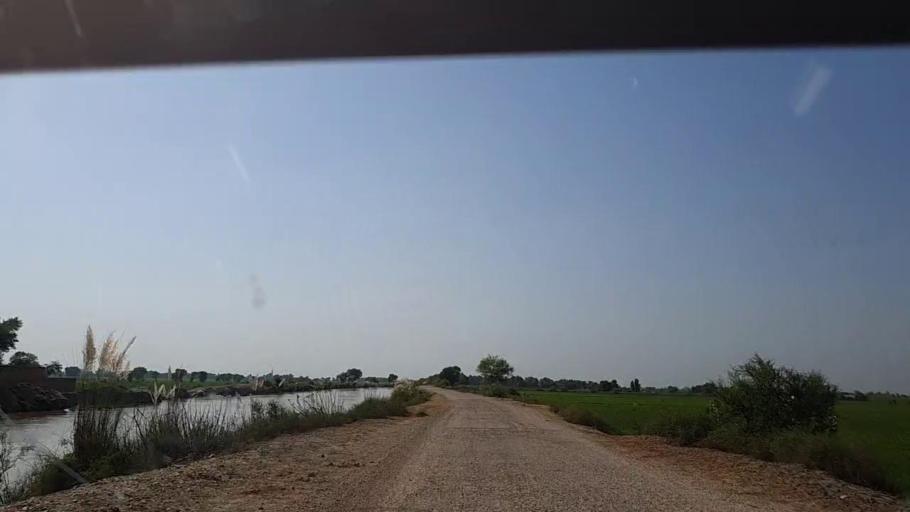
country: PK
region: Sindh
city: Ghauspur
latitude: 28.1862
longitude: 69.0678
